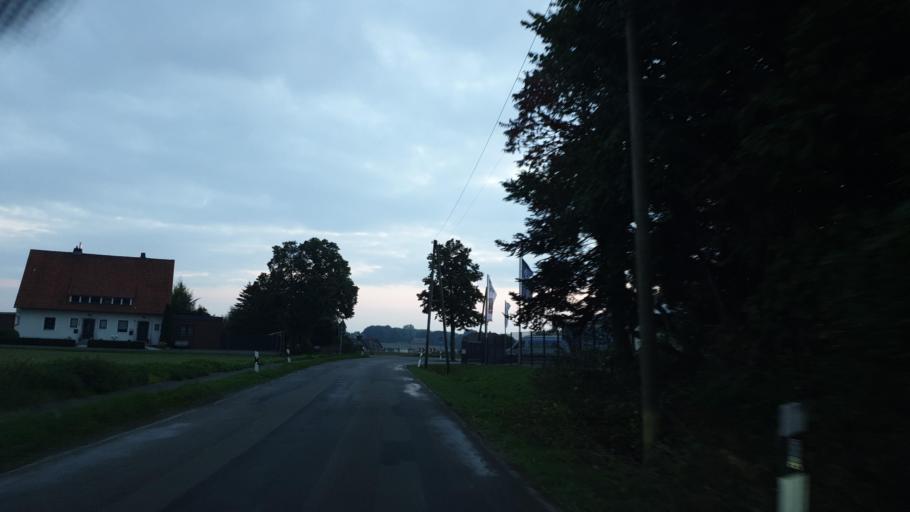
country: DE
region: North Rhine-Westphalia
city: Loehne
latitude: 52.2492
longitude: 8.7339
